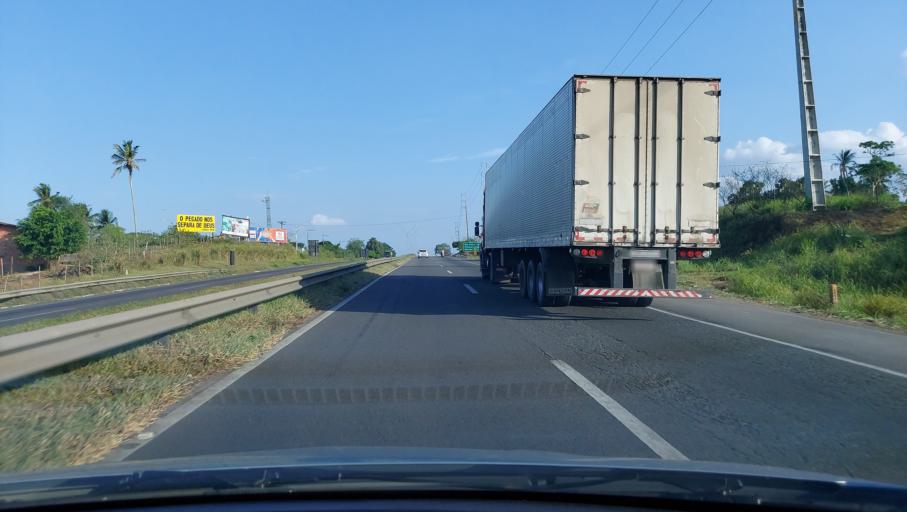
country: BR
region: Bahia
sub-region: Conceicao Do Jacuipe
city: Conceicao do Jacuipe
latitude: -12.3659
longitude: -38.8182
